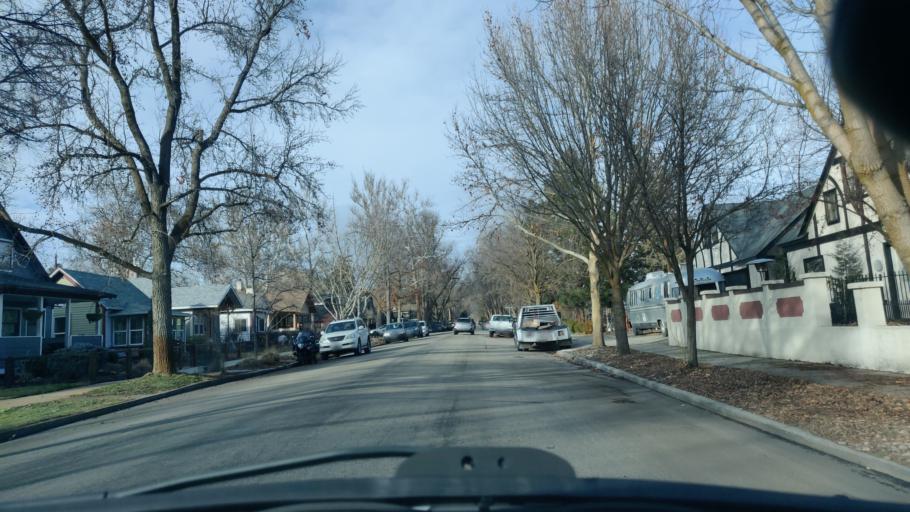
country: US
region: Idaho
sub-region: Ada County
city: Boise
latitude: 43.6311
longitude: -116.1987
